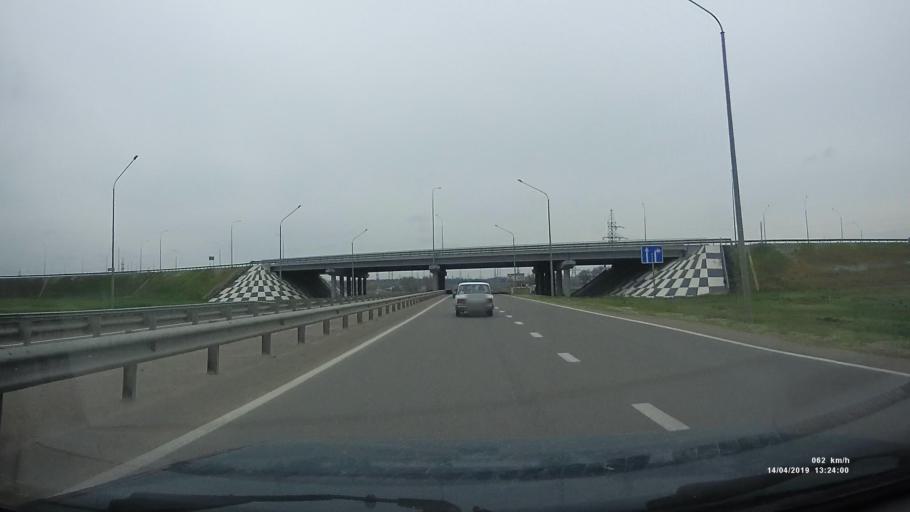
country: RU
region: Rostov
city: Kuleshovka
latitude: 47.0845
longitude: 39.4926
